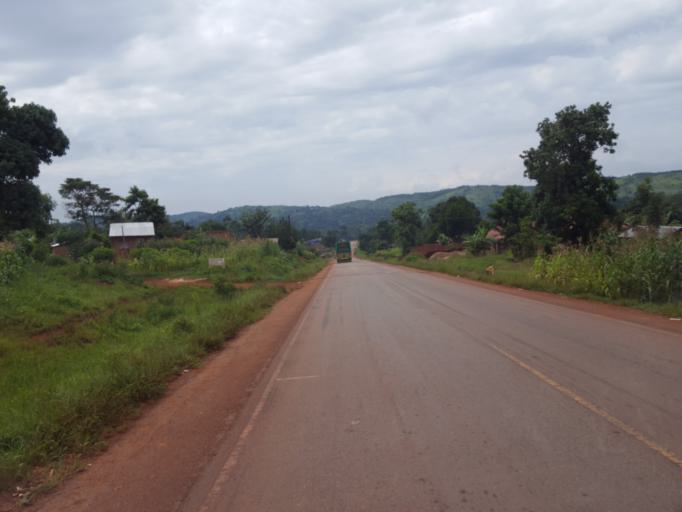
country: UG
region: Central Region
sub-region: Mityana District
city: Mityana
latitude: 0.6359
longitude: 32.1073
